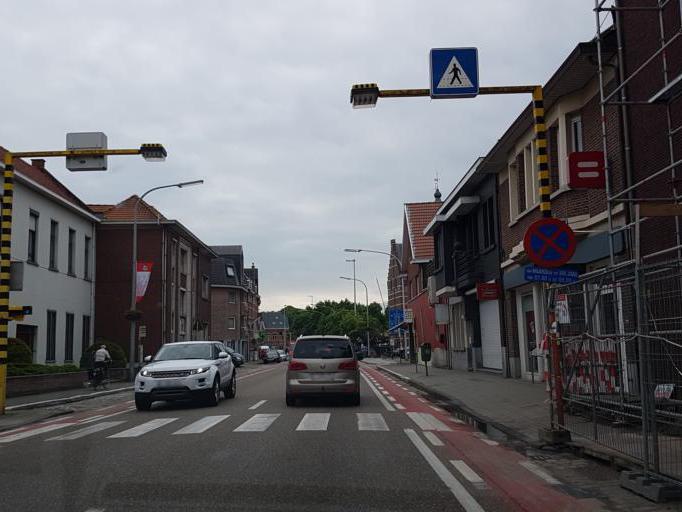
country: BE
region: Flanders
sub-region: Provincie Antwerpen
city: Oostmalle
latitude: 51.3028
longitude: 4.7348
